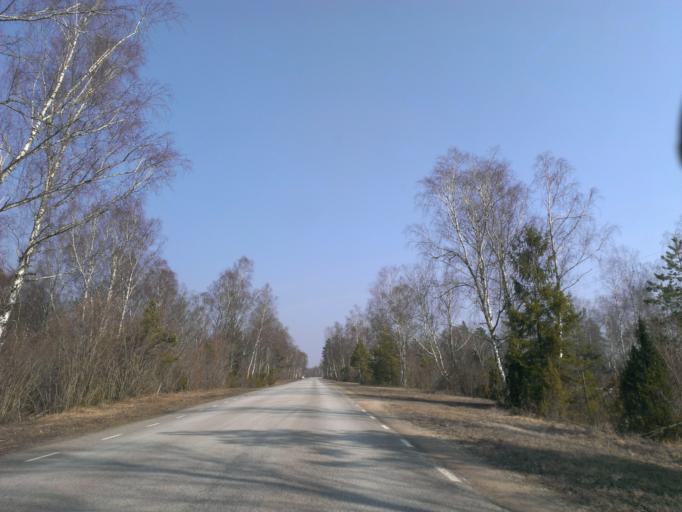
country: EE
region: Saare
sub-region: Kuressaare linn
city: Kuressaare
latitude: 58.2704
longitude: 22.6133
